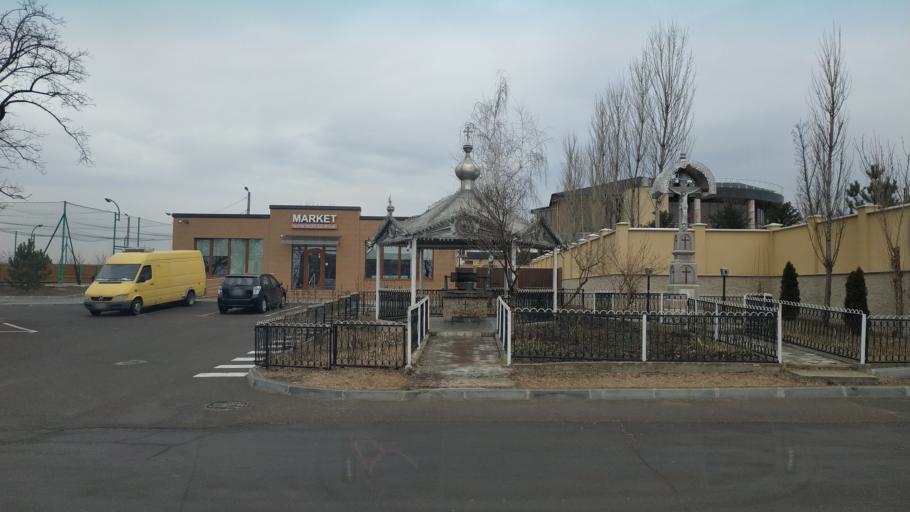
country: MD
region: Chisinau
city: Singera
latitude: 46.9202
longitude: 28.9610
